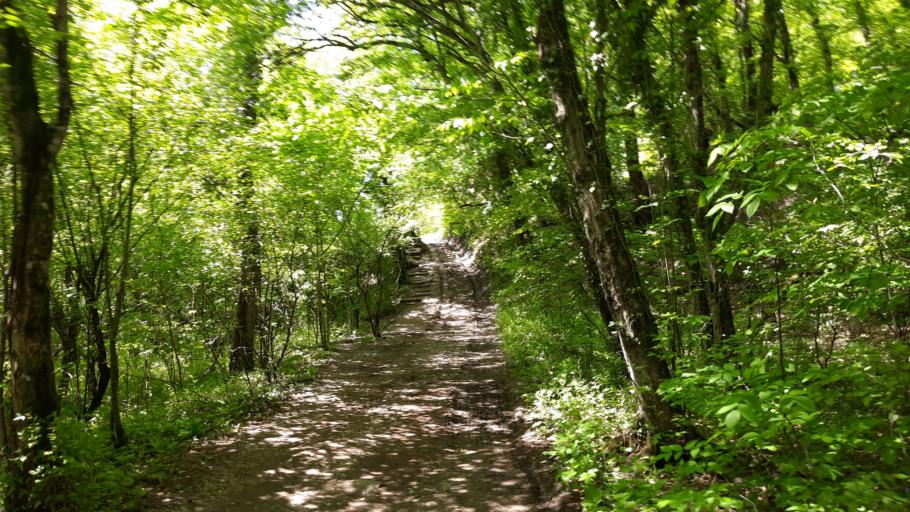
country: RU
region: Krasnodarskiy
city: Divnomorskoye
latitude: 44.5627
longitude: 38.2588
